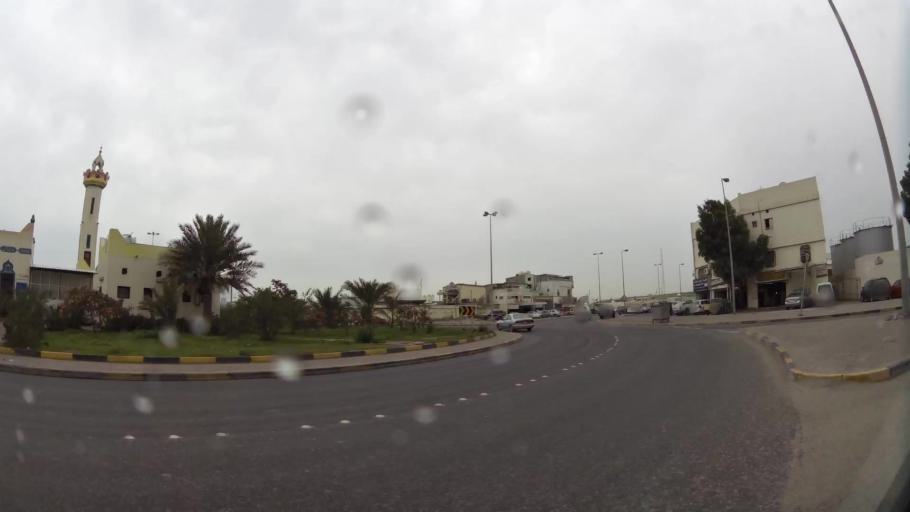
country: BH
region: Northern
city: Madinat `Isa
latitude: 26.1852
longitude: 50.5269
